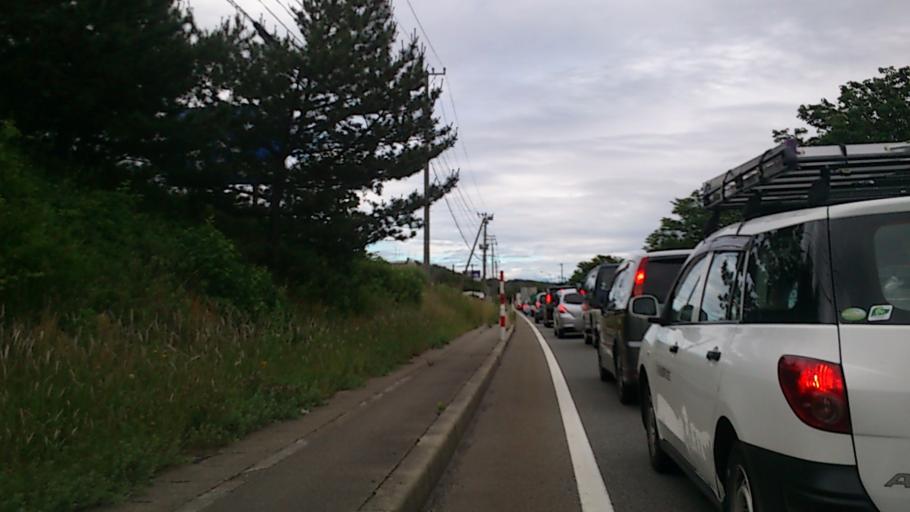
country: JP
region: Akita
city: Akita Shi
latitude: 39.6335
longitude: 140.0652
